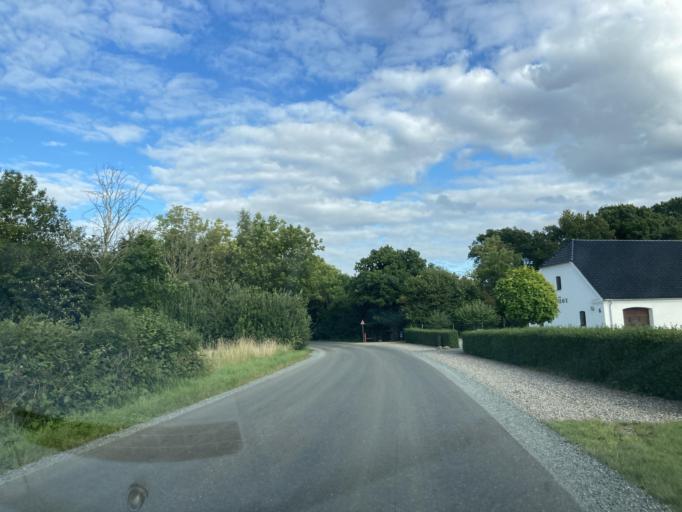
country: DK
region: South Denmark
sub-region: Kolding Kommune
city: Sonder Bjert
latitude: 55.4599
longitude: 9.6446
